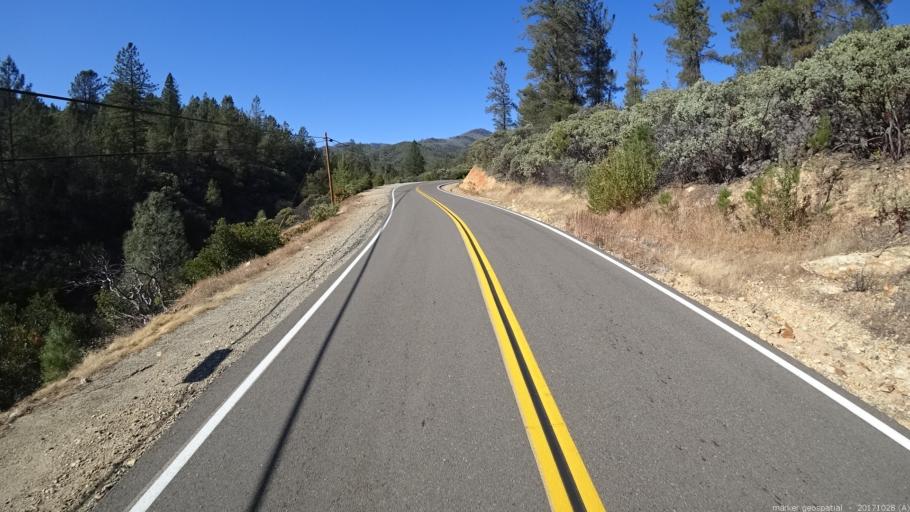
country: US
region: California
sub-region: Shasta County
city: Shasta
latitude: 40.6580
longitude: -122.4678
